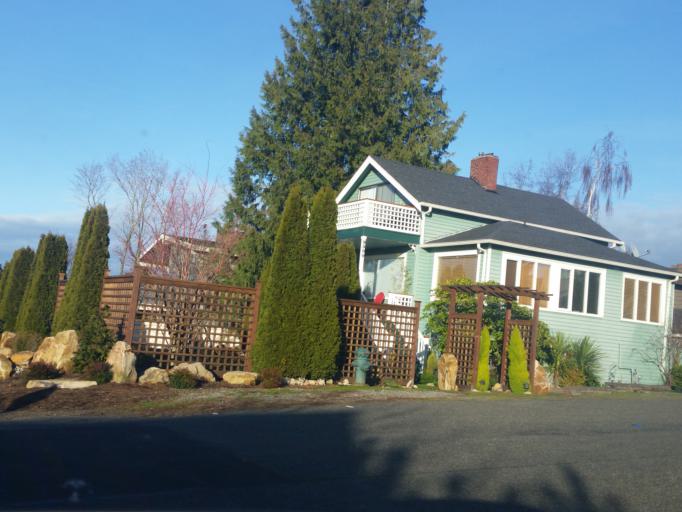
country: US
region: Washington
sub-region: King County
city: Shoreline
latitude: 47.6982
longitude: -122.3830
